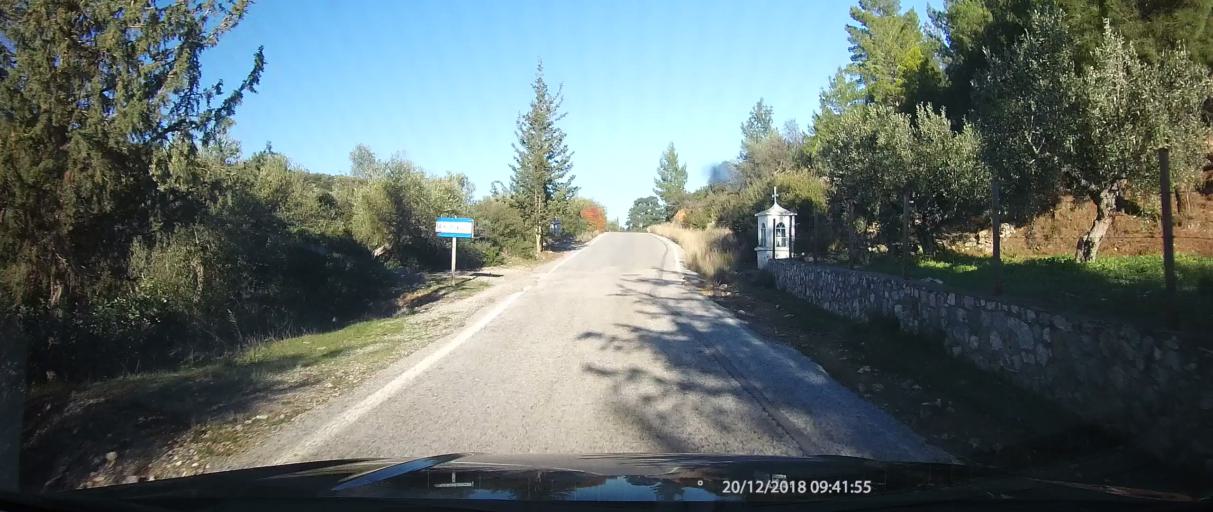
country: GR
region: Peloponnese
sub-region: Nomos Lakonias
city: Yerakion
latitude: 36.9544
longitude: 22.7600
